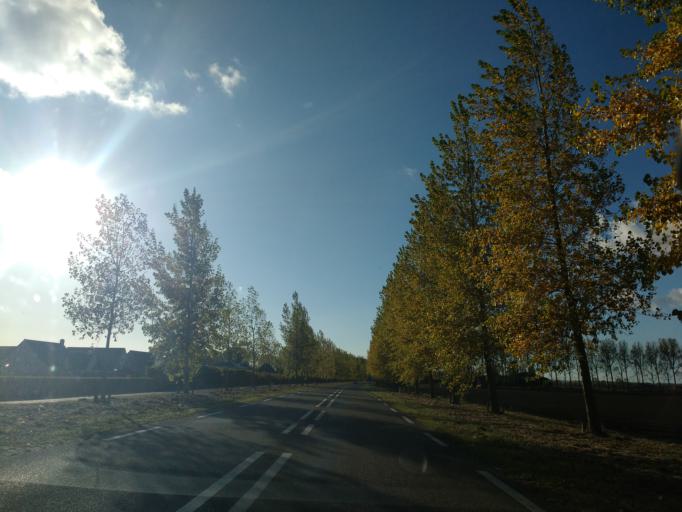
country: NL
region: Zeeland
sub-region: Gemeente Vlissingen
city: Vlissingen
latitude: 51.3917
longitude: 3.5482
